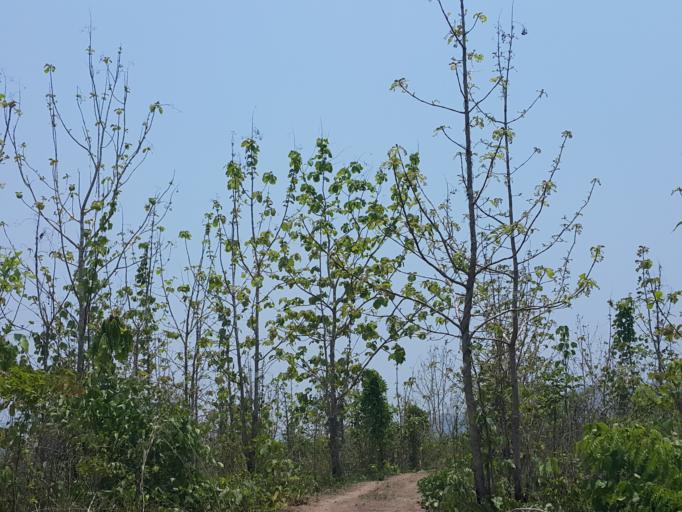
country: TH
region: Kanchanaburi
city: Sai Yok
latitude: 14.2406
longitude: 98.8717
